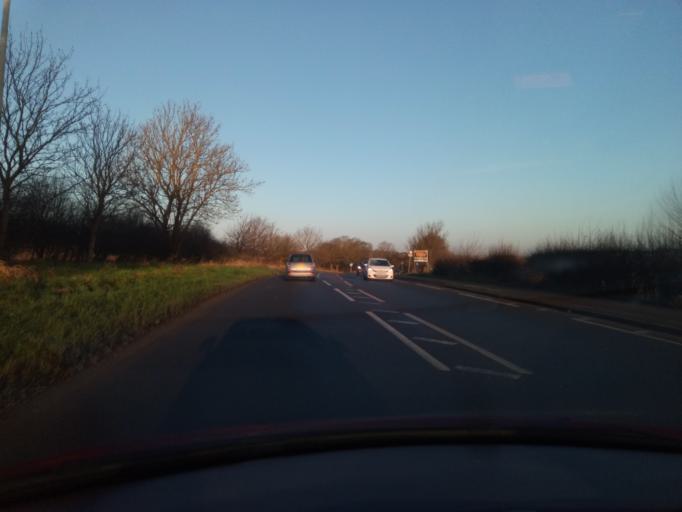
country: GB
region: England
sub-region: Leicestershire
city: Hathern
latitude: 52.7860
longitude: -1.2476
